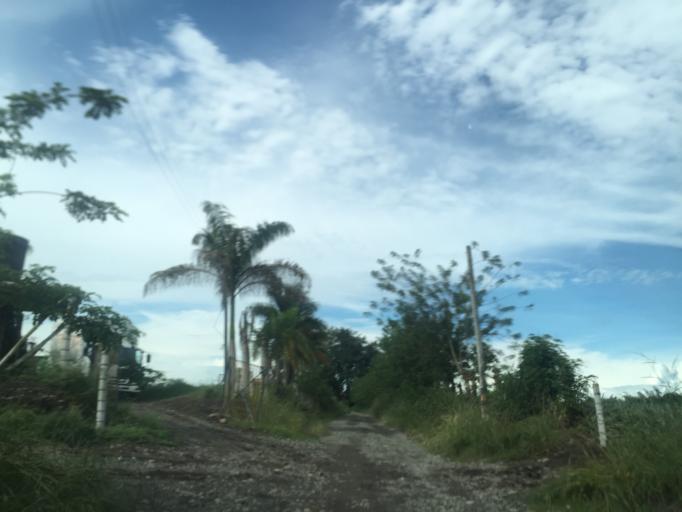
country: CO
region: Quindio
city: La Tebaida
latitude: 4.4716
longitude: -75.8387
